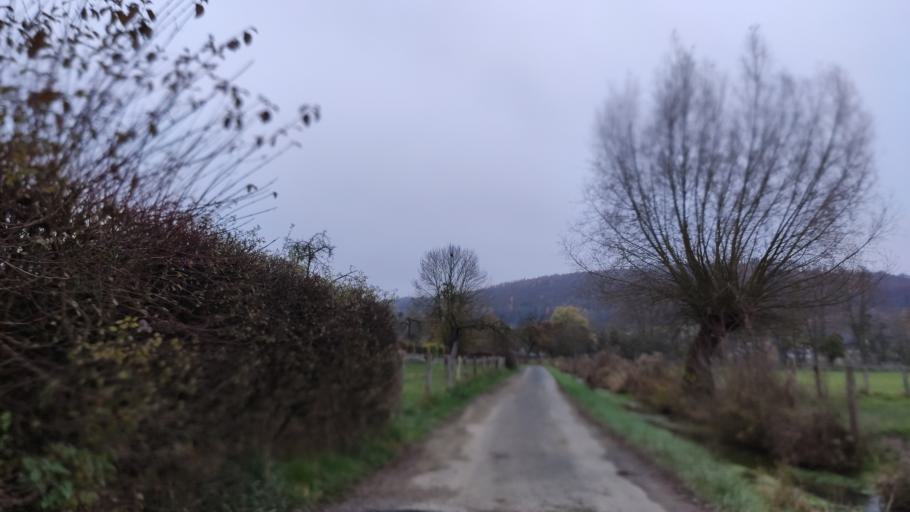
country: DE
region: North Rhine-Westphalia
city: Beverungen
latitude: 51.7091
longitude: 9.2894
